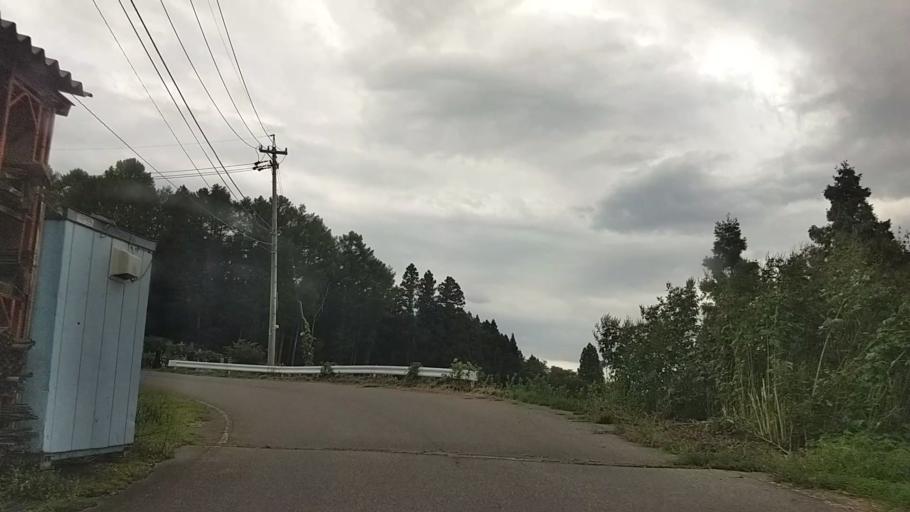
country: JP
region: Nagano
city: Iiyama
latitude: 36.8163
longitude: 138.3654
